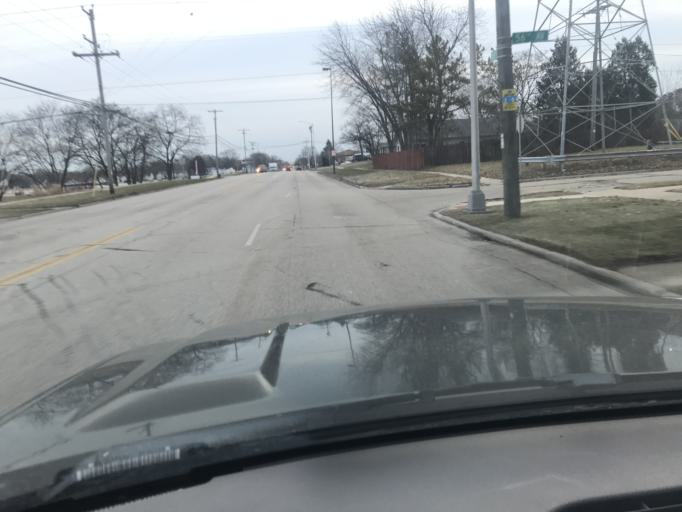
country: US
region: Wisconsin
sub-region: Kenosha County
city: Kenosha
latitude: 42.5886
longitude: -87.8757
